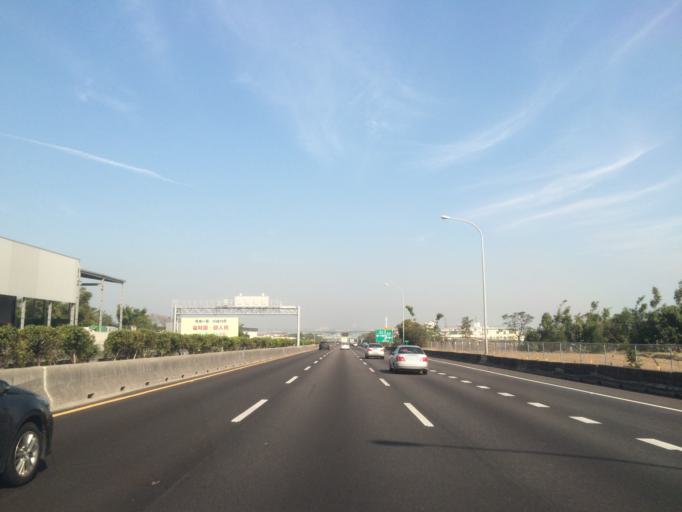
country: TW
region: Taiwan
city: Fengyuan
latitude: 24.2562
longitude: 120.6912
